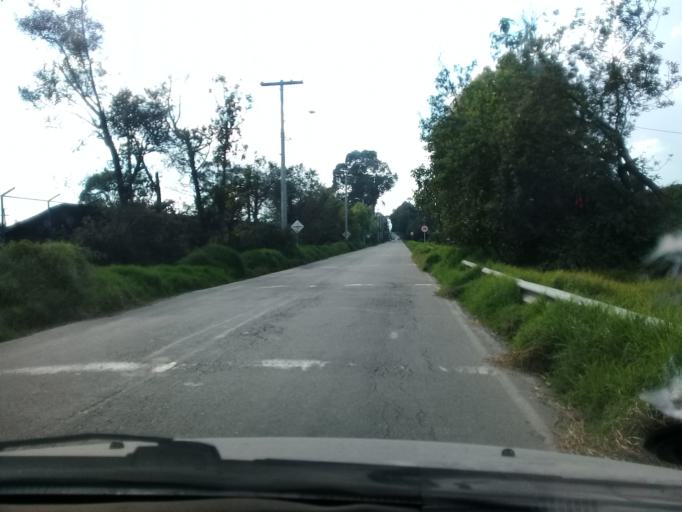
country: CO
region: Cundinamarca
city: El Rosal
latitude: 4.8191
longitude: -74.2305
